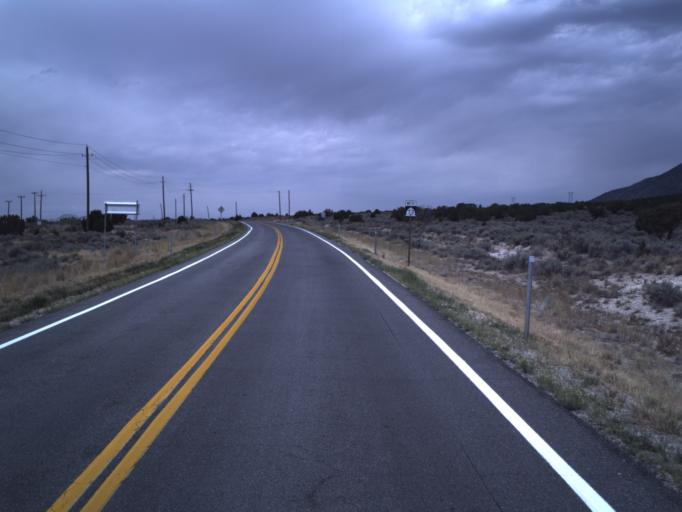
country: US
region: Utah
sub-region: Tooele County
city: Tooele
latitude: 40.3249
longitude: -112.2885
